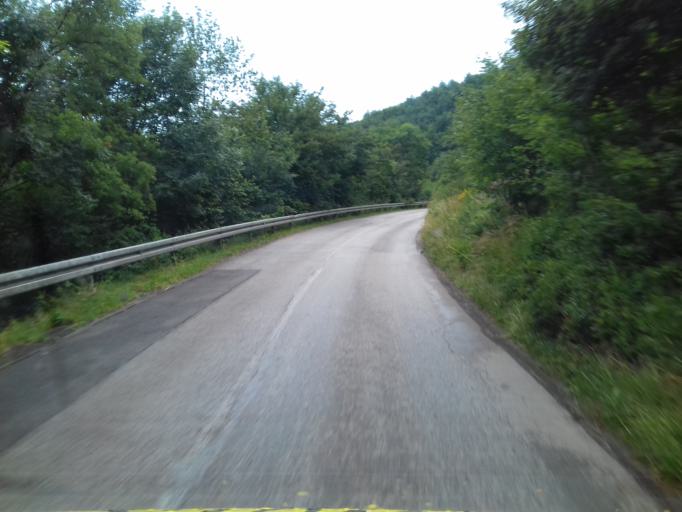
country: BA
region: Federation of Bosnia and Herzegovina
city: Visoko
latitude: 43.9610
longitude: 18.1728
